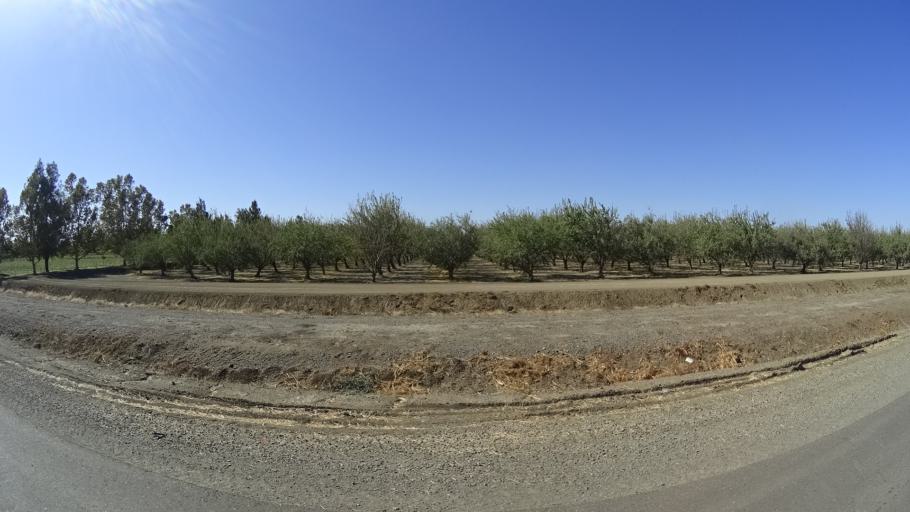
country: US
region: California
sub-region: Yolo County
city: Woodland
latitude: 38.6082
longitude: -121.8030
